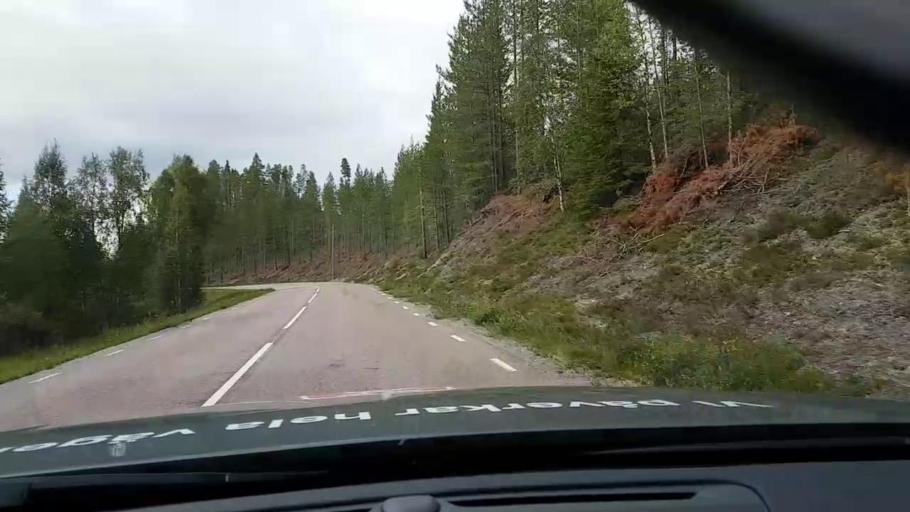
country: SE
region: Vaesterbotten
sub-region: Asele Kommun
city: Asele
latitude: 63.8653
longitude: 17.3656
